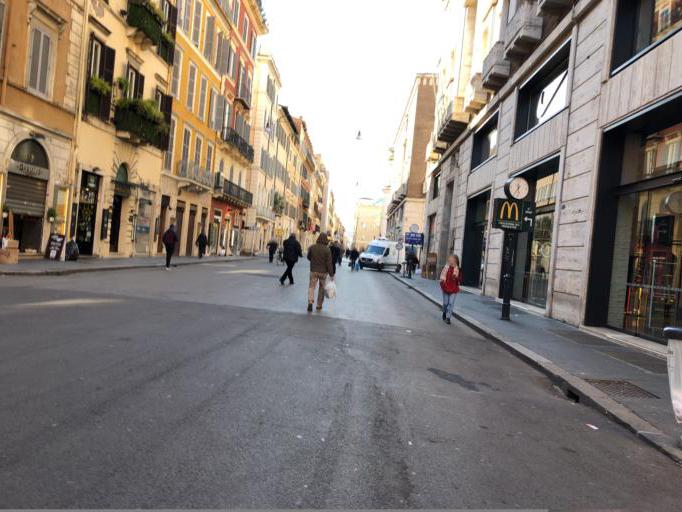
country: VA
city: Vatican City
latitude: 41.9070
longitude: 12.4779
